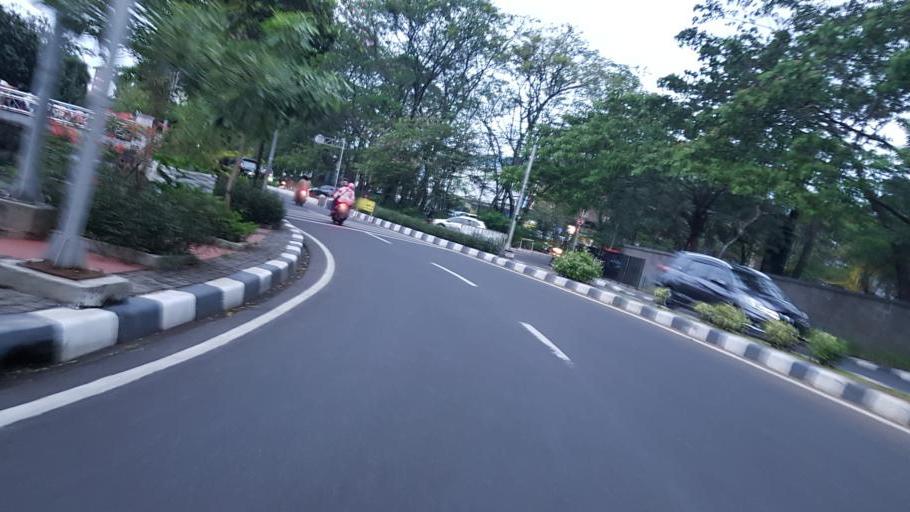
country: ID
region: West Java
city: Ciputat
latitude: -6.1871
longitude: 106.7383
